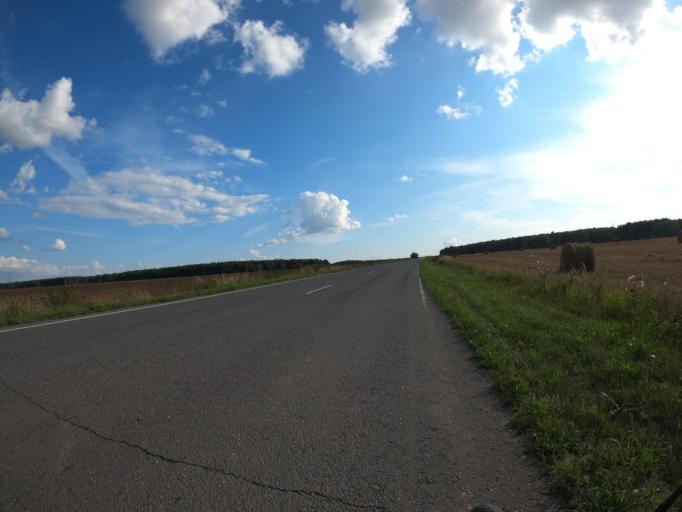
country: RU
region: Moskovskaya
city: Meshcherino
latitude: 55.1764
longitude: 38.4697
